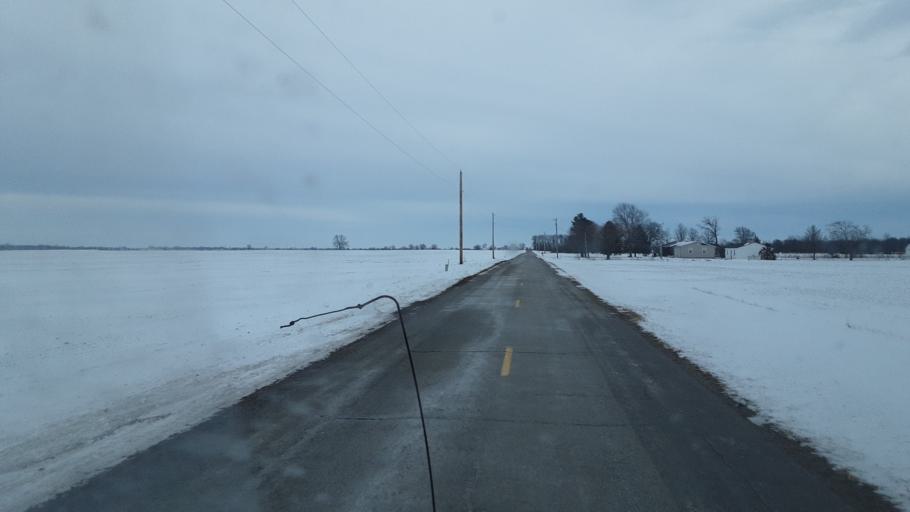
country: US
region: Ohio
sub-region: Madison County
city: Bethel
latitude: 39.7122
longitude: -83.3663
